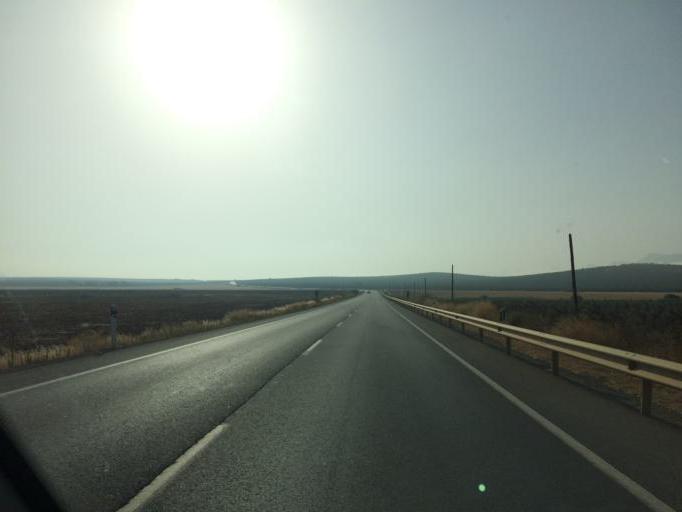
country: ES
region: Andalusia
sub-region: Provincia de Malaga
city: Humilladero
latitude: 37.0530
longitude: -4.7633
